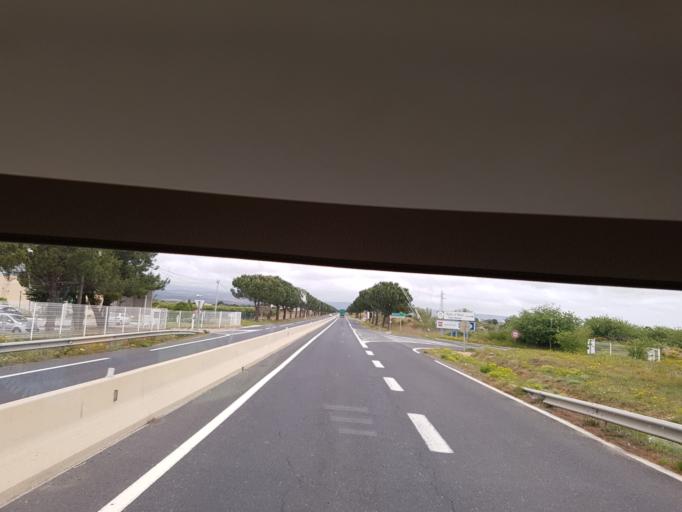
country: FR
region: Languedoc-Roussillon
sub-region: Departement des Pyrenees-Orientales
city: Rivesaltes
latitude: 42.7829
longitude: 2.9046
